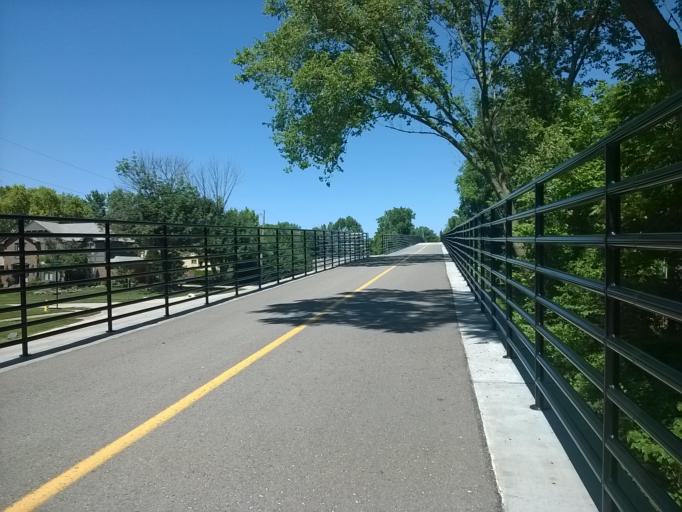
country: US
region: Indiana
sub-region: Hamilton County
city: Carmel
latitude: 39.9985
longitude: -86.1364
